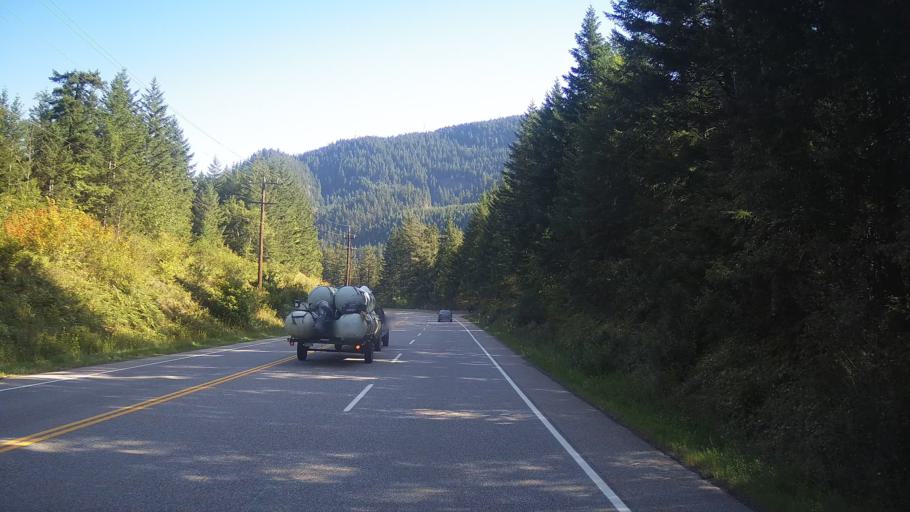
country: CA
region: British Columbia
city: Hope
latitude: 49.6518
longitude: -121.4069
